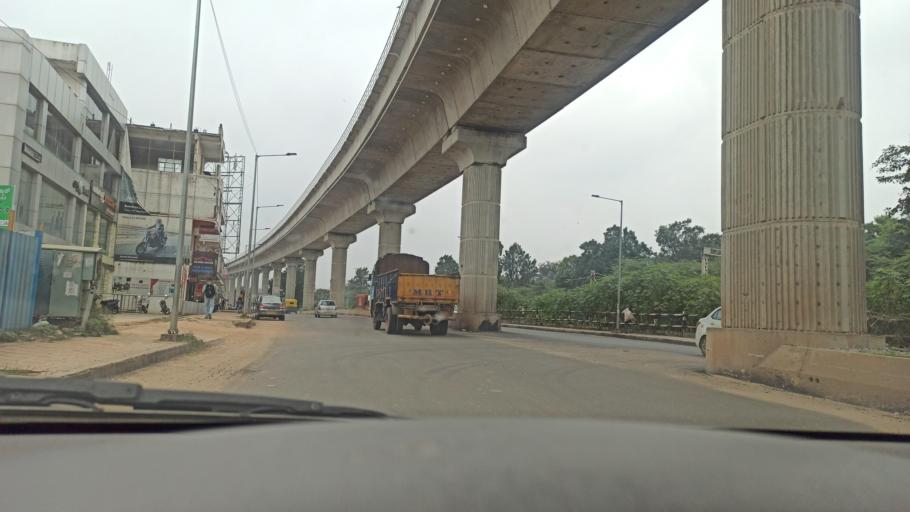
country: IN
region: Karnataka
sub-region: Bangalore Urban
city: Bangalore
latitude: 13.0001
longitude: 77.6863
